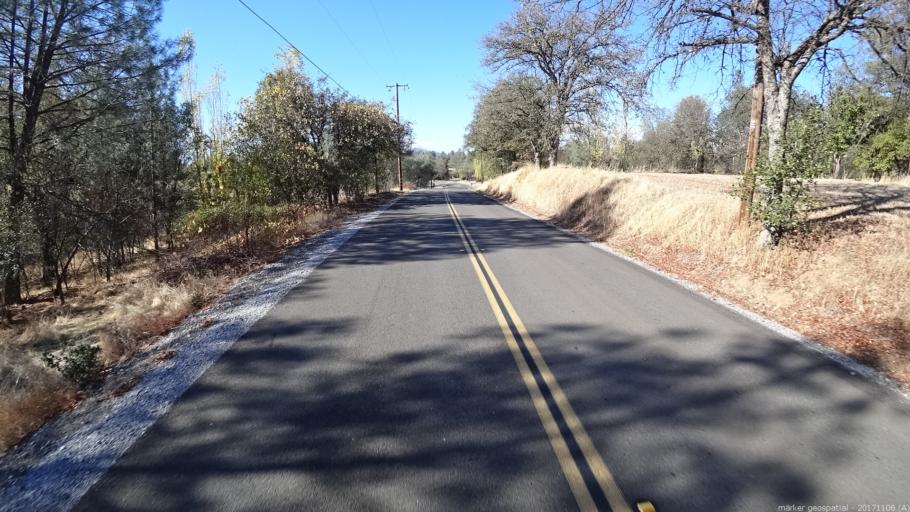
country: US
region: California
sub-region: Shasta County
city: Bella Vista
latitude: 40.6218
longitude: -122.2759
